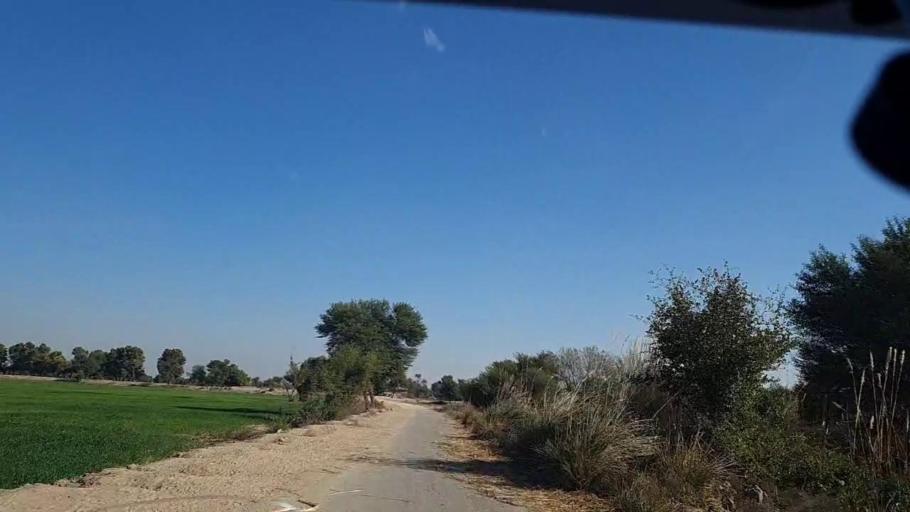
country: PK
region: Sindh
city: Khanpur
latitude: 27.6158
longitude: 69.4475
